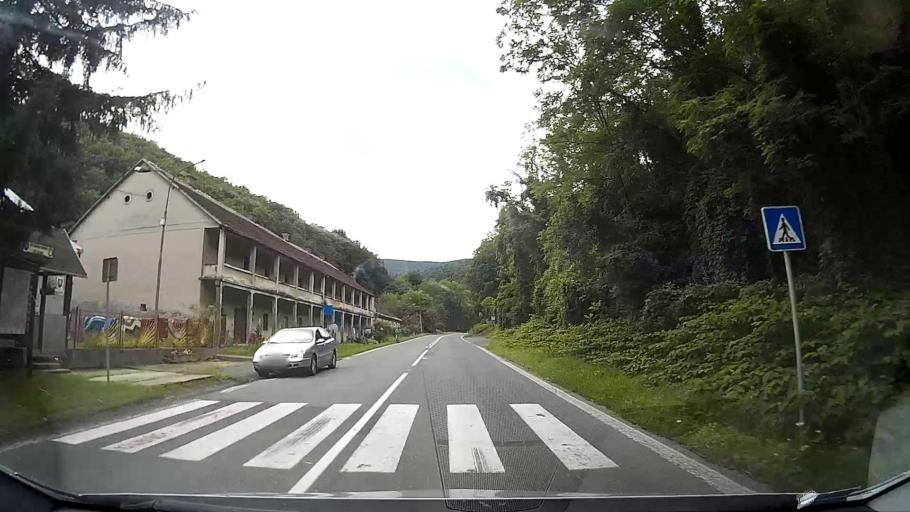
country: HU
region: Nograd
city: Somoskoujfalu
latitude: 48.1922
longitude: 19.8166
